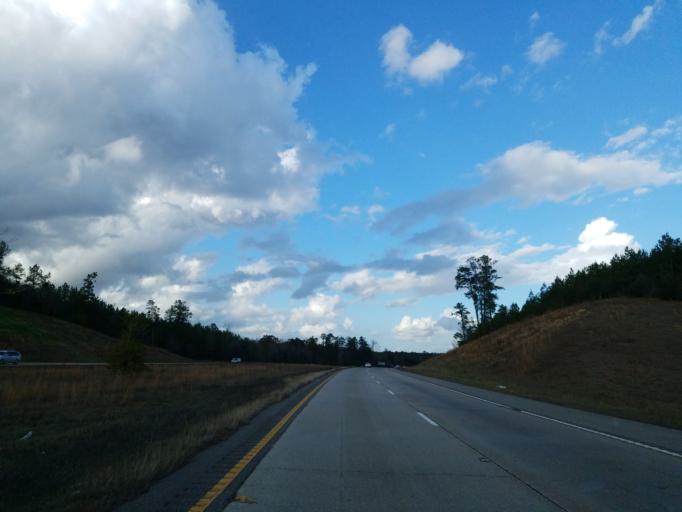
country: US
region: Mississippi
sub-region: Forrest County
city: Rawls Springs
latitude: 31.4835
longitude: -89.3236
